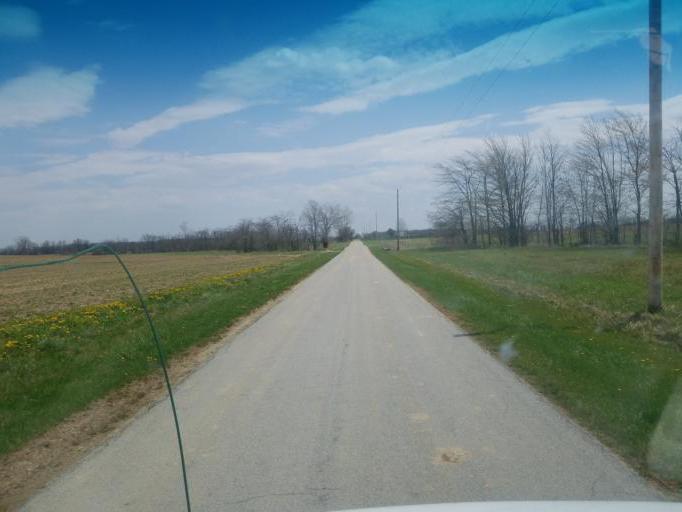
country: US
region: Ohio
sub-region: Hardin County
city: Forest
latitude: 40.7742
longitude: -83.4468
